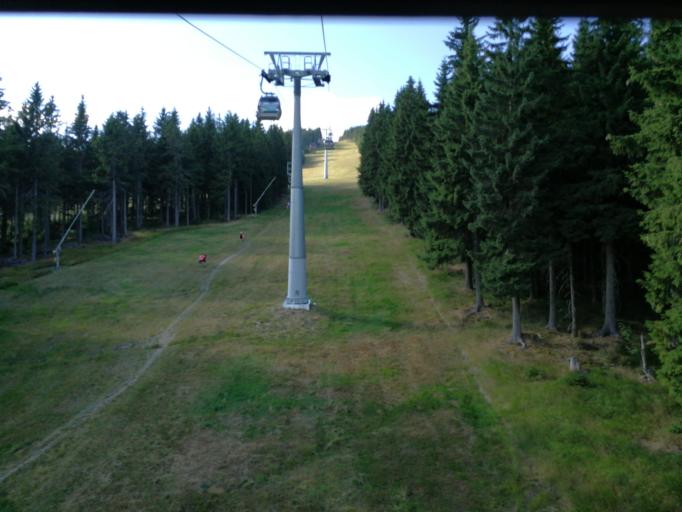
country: CZ
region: Kralovehradecky
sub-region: Okres Trutnov
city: Rudnik
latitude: 50.6405
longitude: 15.7603
